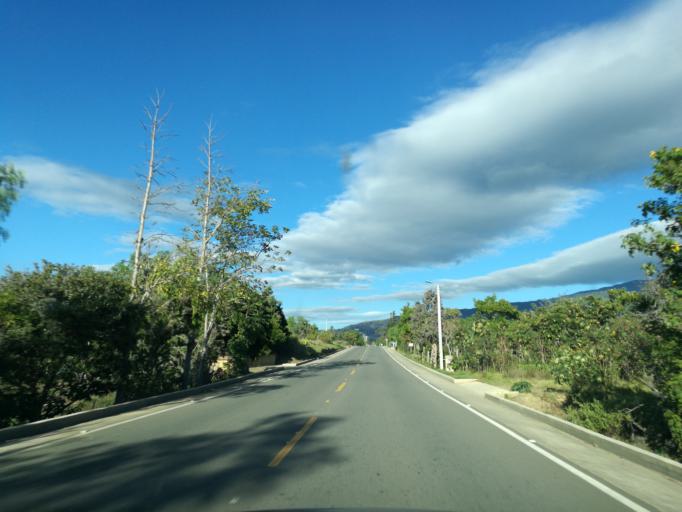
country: CO
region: Boyaca
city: Sutamarchan
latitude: 5.6235
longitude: -73.5956
